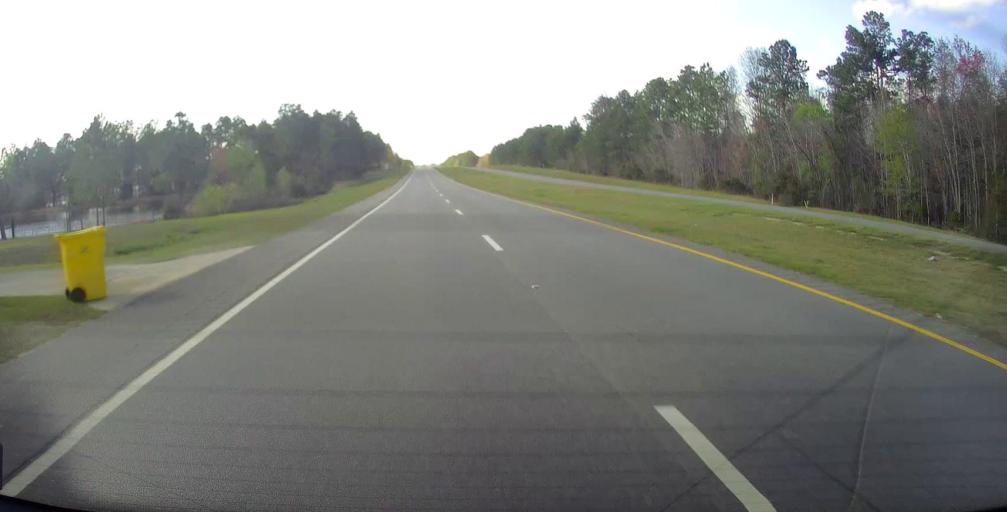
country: US
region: Georgia
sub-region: Telfair County
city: Helena
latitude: 32.0877
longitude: -82.9354
